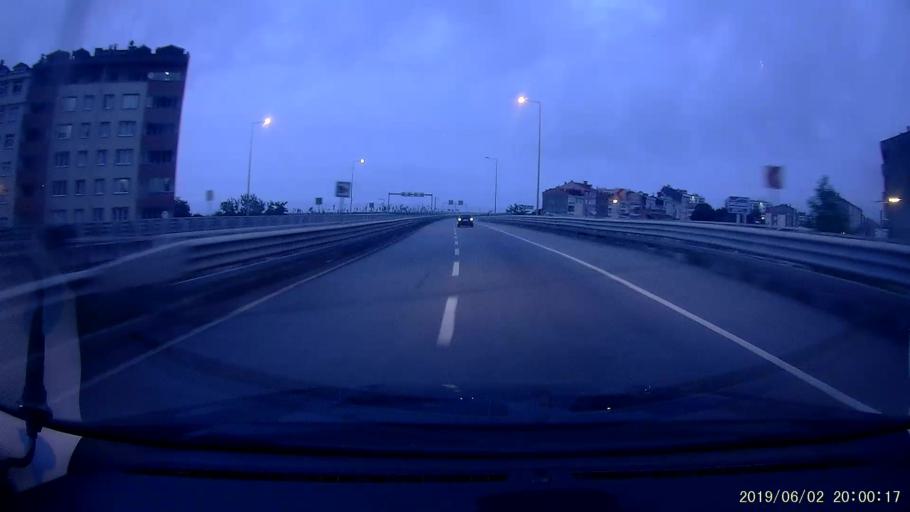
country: TR
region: Giresun
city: Tirebolu
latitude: 41.0055
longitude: 38.8371
